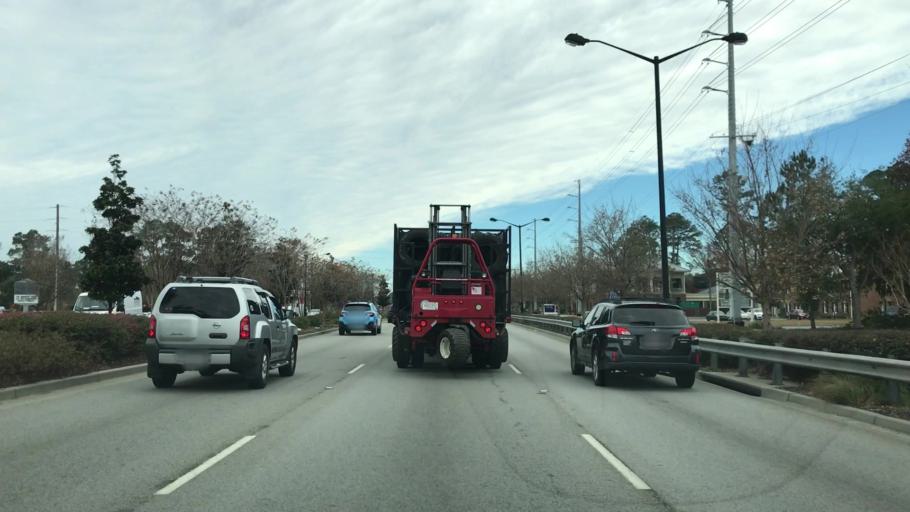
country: US
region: South Carolina
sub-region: Charleston County
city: Mount Pleasant
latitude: 32.8115
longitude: -79.8658
